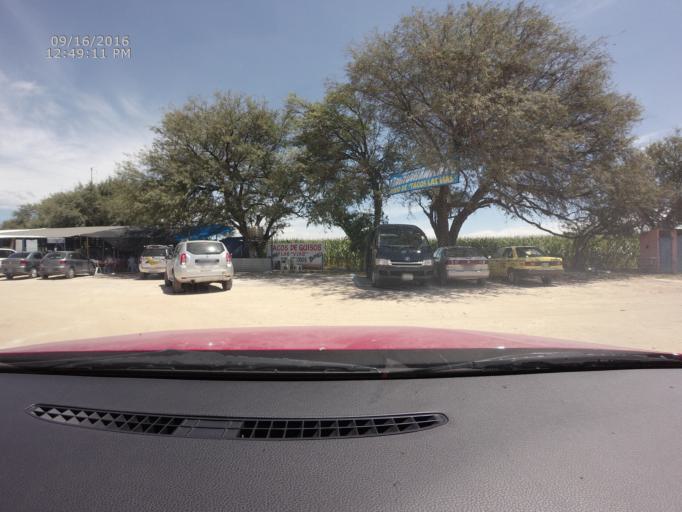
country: MX
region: Queretaro
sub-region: Colon
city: Purisima de Cubos (La Purisima)
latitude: 20.5994
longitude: -100.1735
